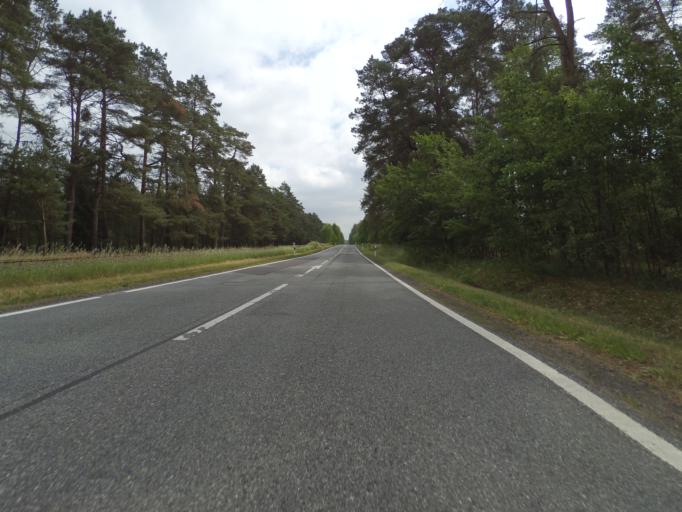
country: DE
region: Mecklenburg-Vorpommern
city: Grabowhofe
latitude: 53.5325
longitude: 12.5056
